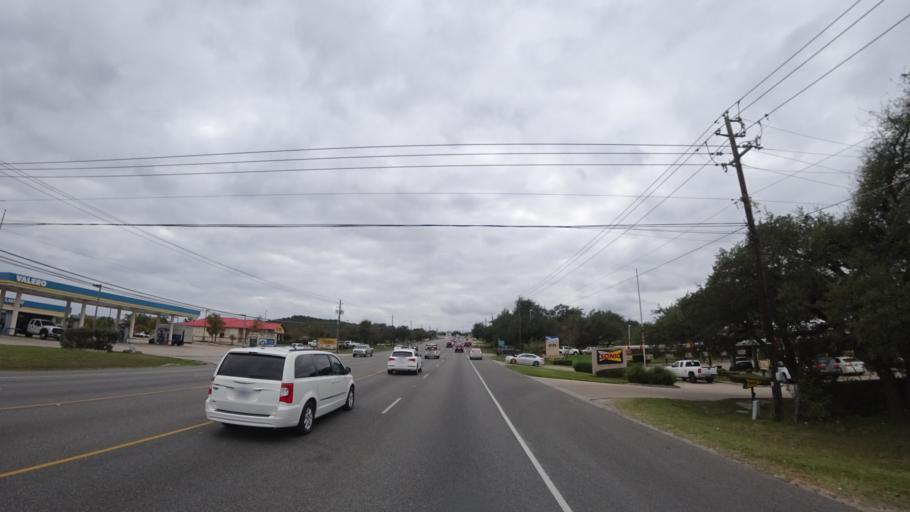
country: US
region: Texas
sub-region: Travis County
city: The Hills
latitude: 30.3434
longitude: -97.9669
